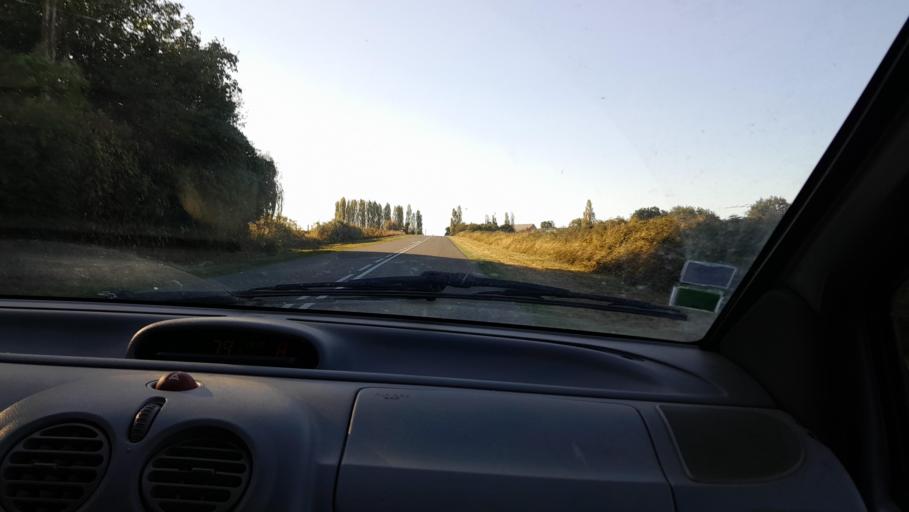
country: FR
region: Pays de la Loire
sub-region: Departement de la Mayenne
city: Craon
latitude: 47.8573
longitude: -0.9719
